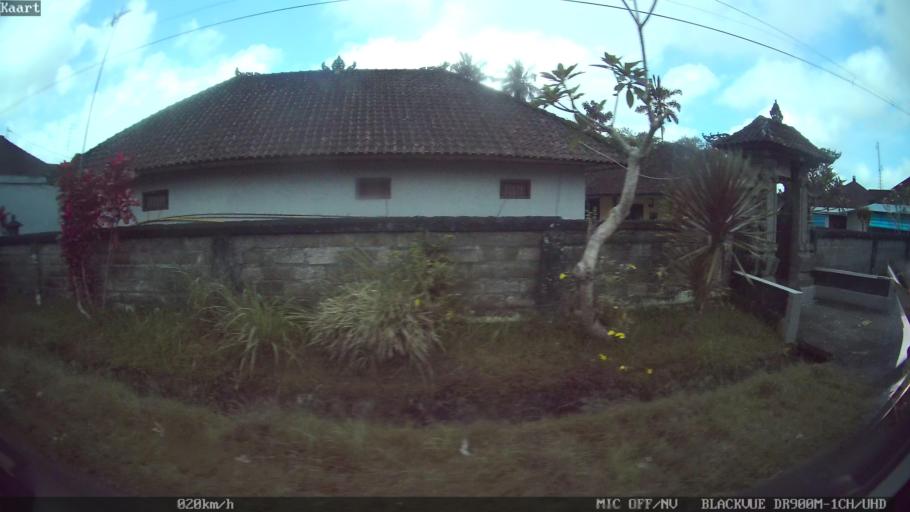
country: ID
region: Bali
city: Banjar Petak
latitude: -8.4443
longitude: 115.3190
